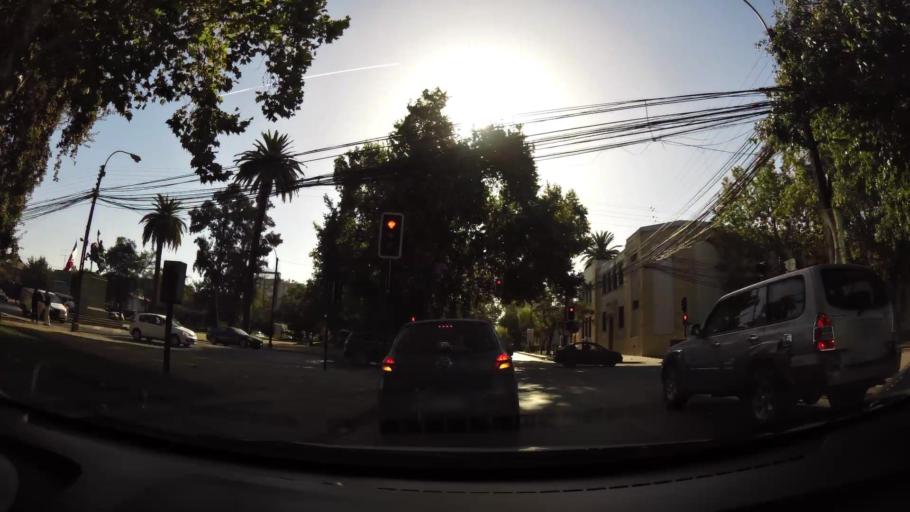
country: CL
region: Maule
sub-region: Provincia de Talca
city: Talca
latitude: -35.4222
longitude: -71.6578
